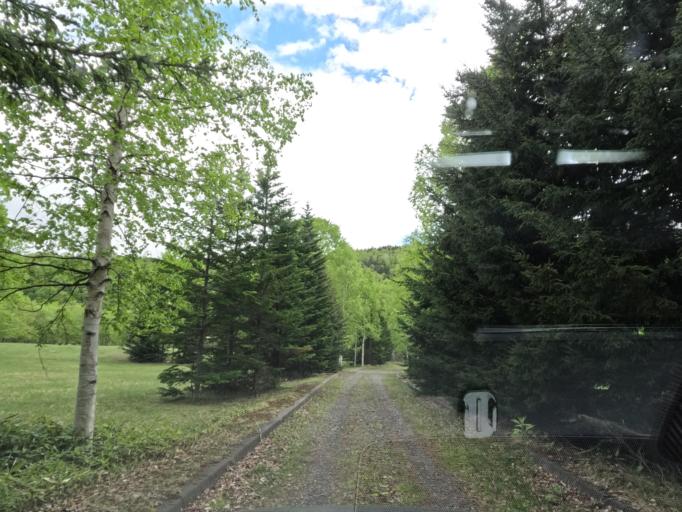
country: JP
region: Hokkaido
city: Kamikawa
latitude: 43.6434
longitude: 143.0224
